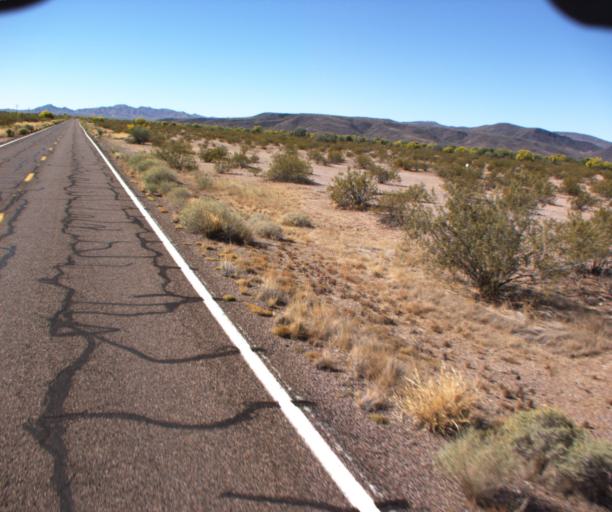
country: US
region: Arizona
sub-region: Pima County
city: Ajo
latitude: 32.5148
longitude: -112.8807
